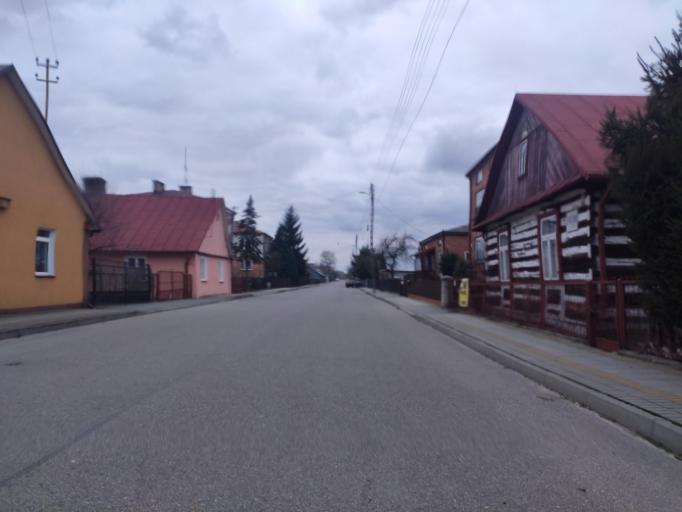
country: PL
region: Lublin Voivodeship
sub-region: Powiat lubartowski
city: Kock
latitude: 51.6391
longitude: 22.4430
